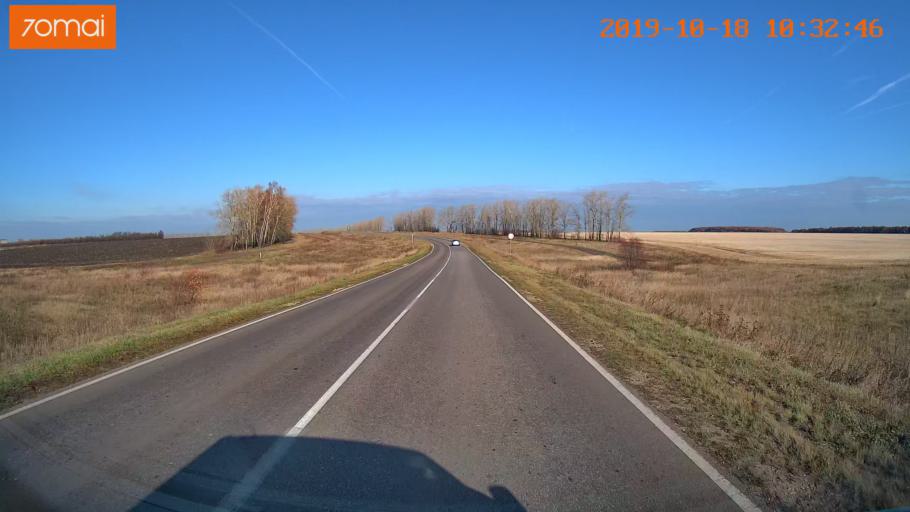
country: RU
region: Tula
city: Kurkino
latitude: 53.4988
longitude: 38.6209
